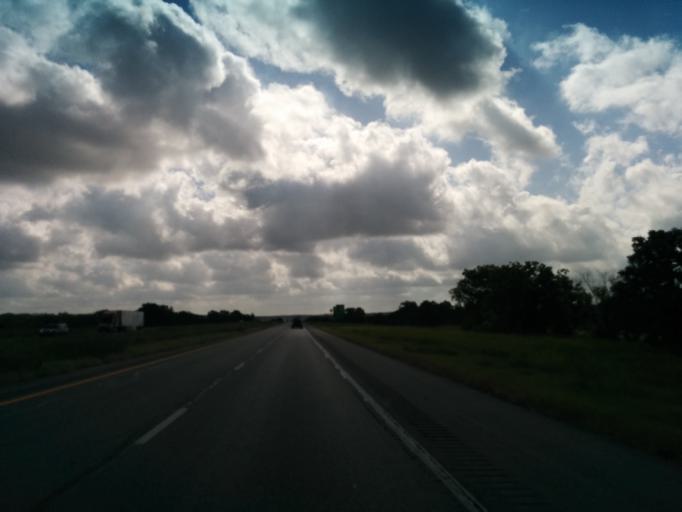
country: US
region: Texas
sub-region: Caldwell County
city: Luling
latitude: 29.6499
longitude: -97.6074
